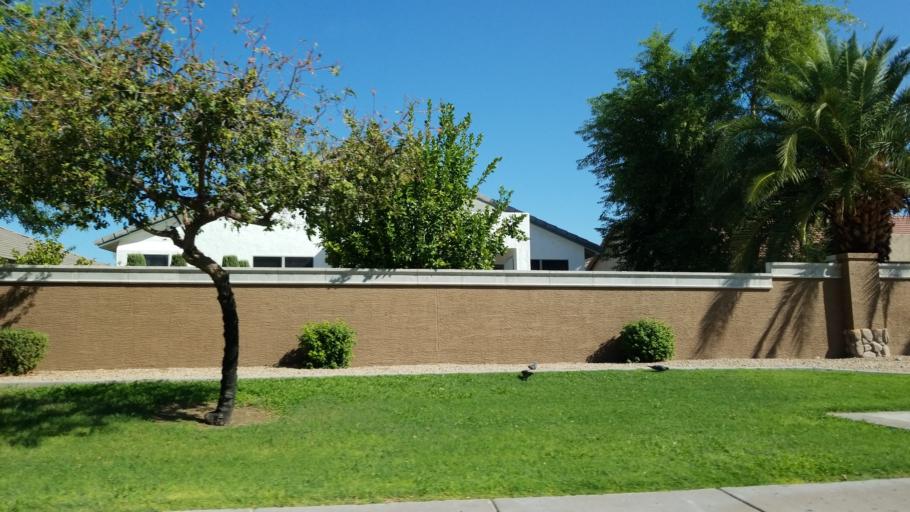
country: US
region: Arizona
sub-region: Maricopa County
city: Peoria
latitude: 33.6603
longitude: -112.1989
